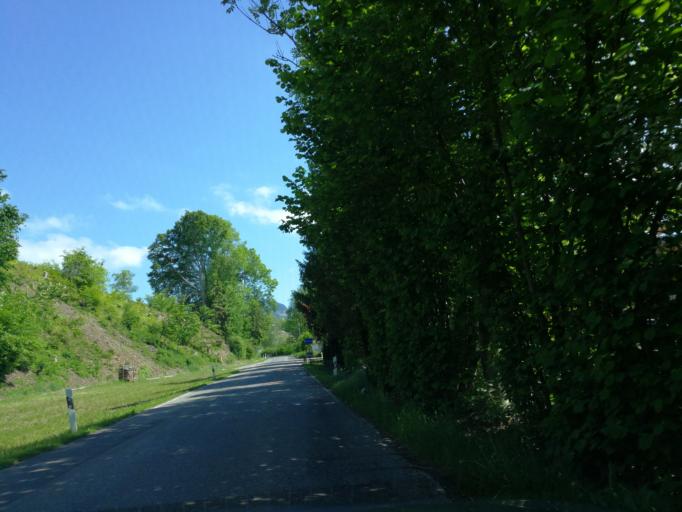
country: CH
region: Saint Gallen
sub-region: Wahlkreis See-Gaster
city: Eschenbach
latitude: 47.2343
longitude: 8.9252
